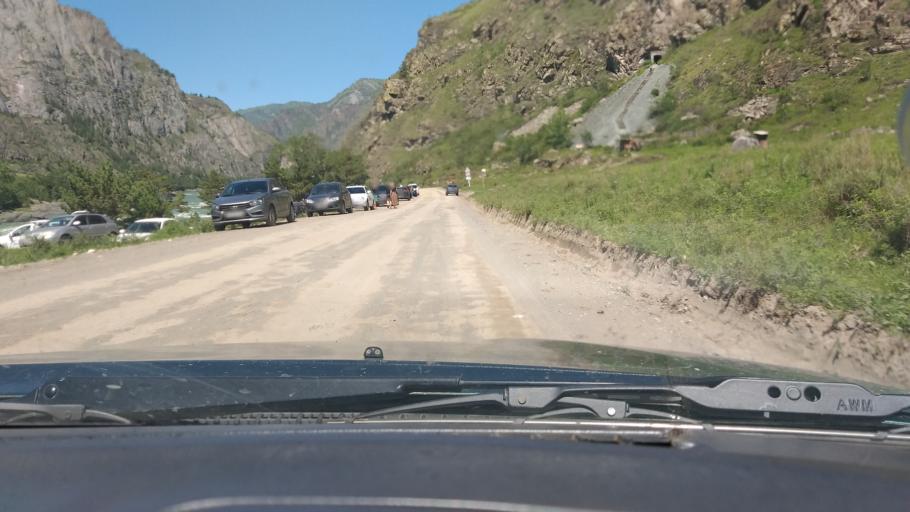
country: RU
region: Altay
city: Chemal
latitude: 51.1994
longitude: 86.0851
